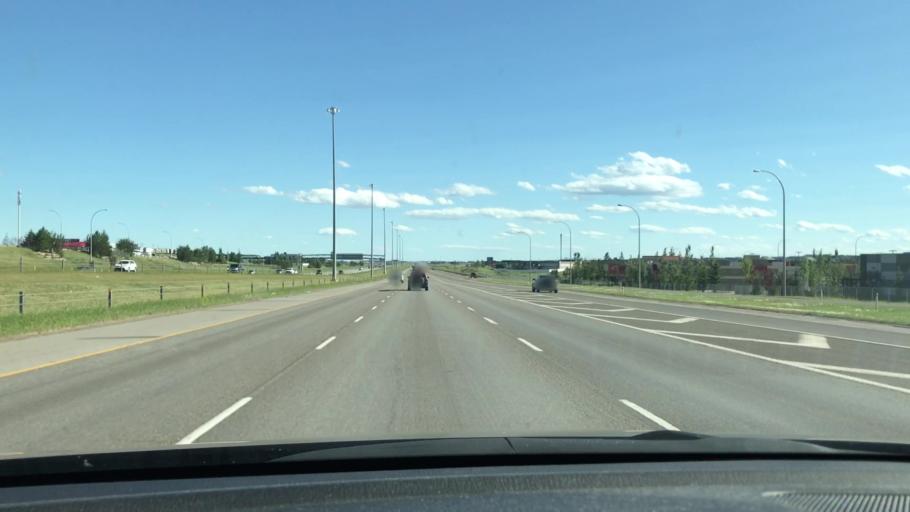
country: CA
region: Alberta
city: Airdrie
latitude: 51.2689
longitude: -114.0017
